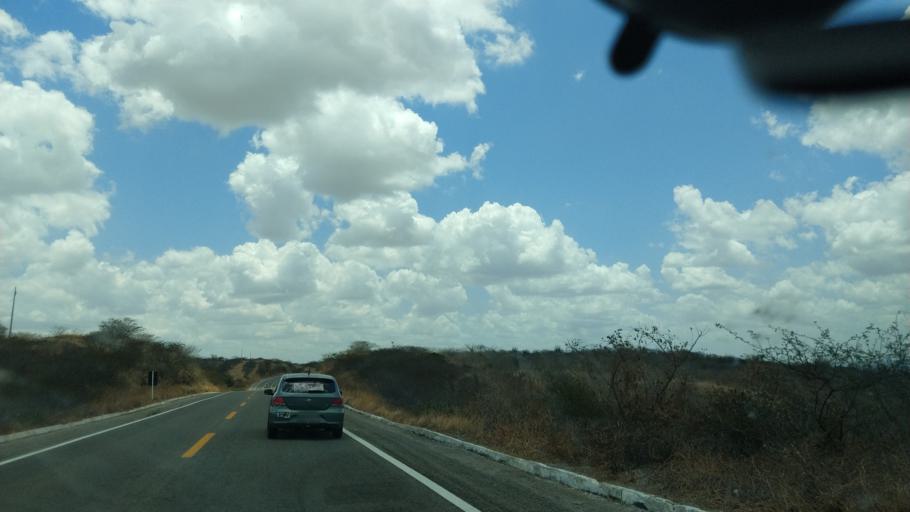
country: BR
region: Rio Grande do Norte
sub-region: Cerro Cora
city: Cerro Cora
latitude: -6.2102
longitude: -36.2977
